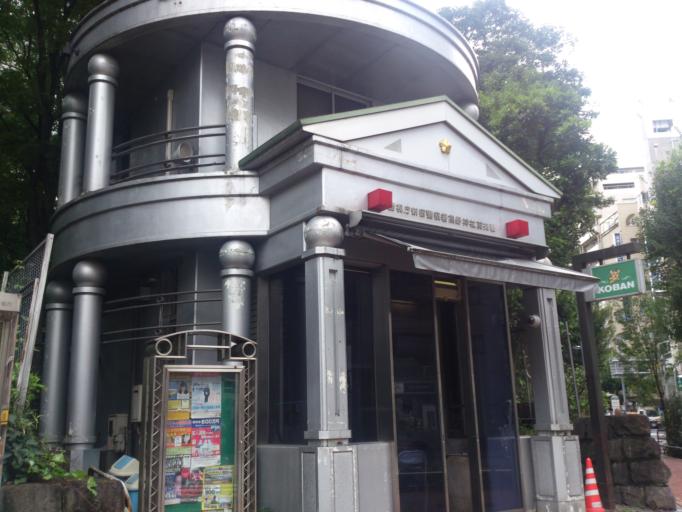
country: JP
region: Tokyo
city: Tokyo
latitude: 35.6911
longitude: 139.6875
